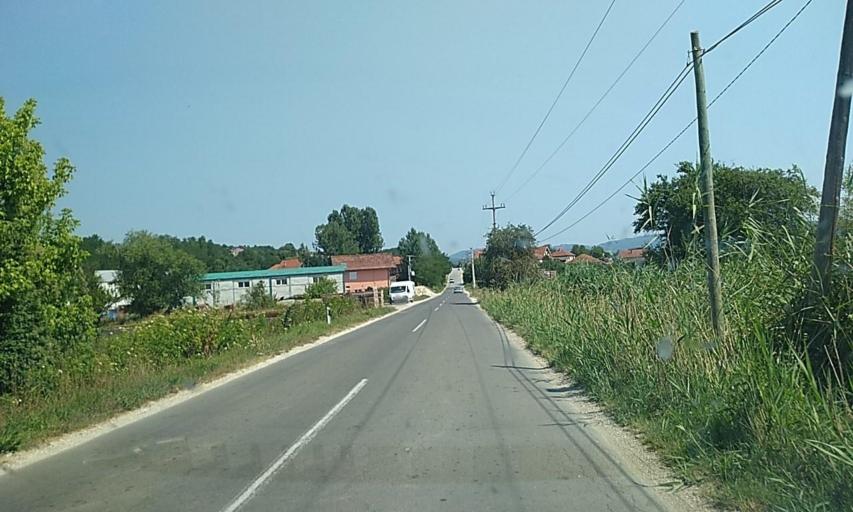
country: RS
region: Central Serbia
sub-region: Pcinjski Okrug
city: Vladicin Han
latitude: 42.6804
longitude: 22.0532
